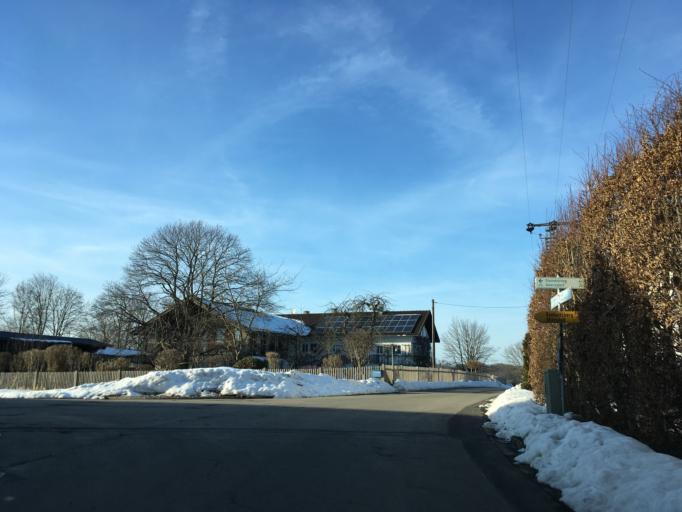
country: DE
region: Bavaria
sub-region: Upper Bavaria
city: Steinhoring
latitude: 48.1095
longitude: 12.0561
